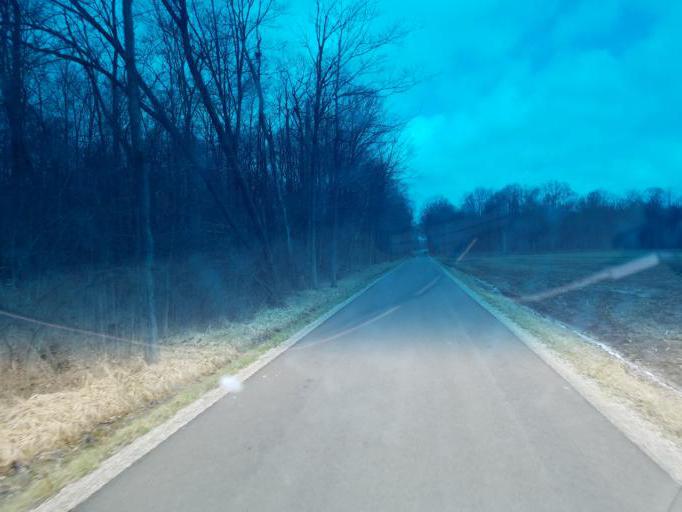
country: US
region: Ohio
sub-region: Crawford County
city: Galion
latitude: 40.7788
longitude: -82.8030
